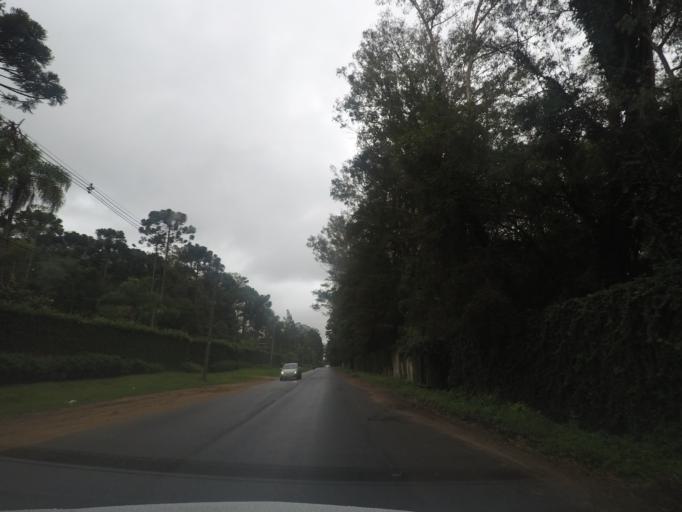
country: BR
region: Parana
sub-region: Pinhais
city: Pinhais
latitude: -25.3898
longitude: -49.1497
